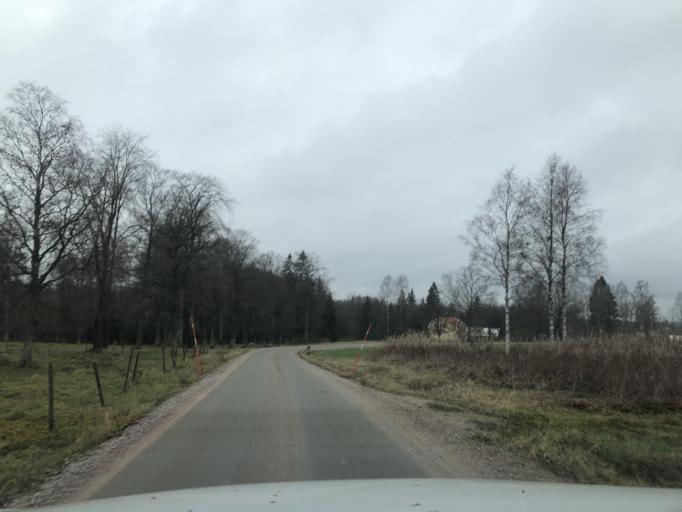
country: SE
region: Vaestra Goetaland
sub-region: Ulricehamns Kommun
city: Ulricehamn
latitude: 57.8588
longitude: 13.6090
